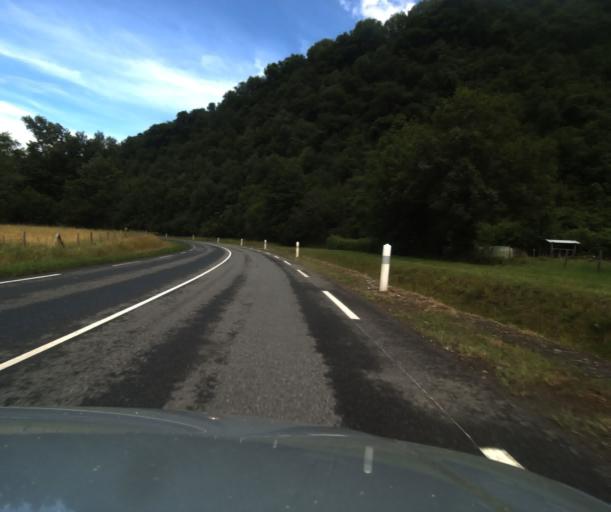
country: FR
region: Midi-Pyrenees
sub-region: Departement des Hautes-Pyrenees
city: Pierrefitte-Nestalas
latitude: 42.9651
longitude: -0.0607
